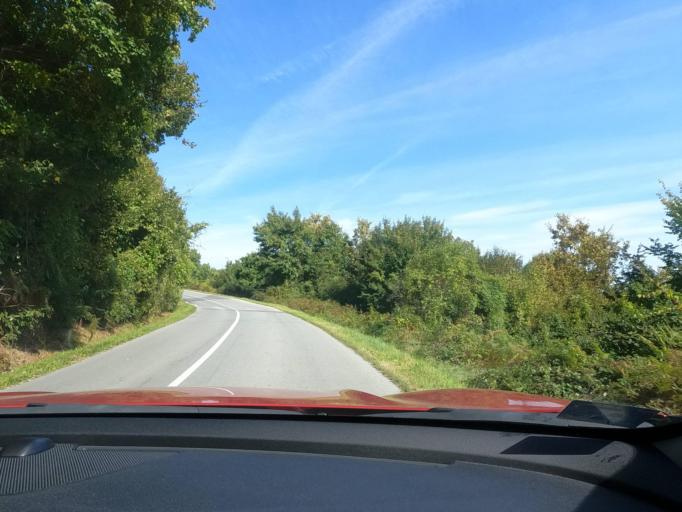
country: HR
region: Sisacko-Moslavacka
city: Petrinja
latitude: 45.3887
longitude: 16.2994
